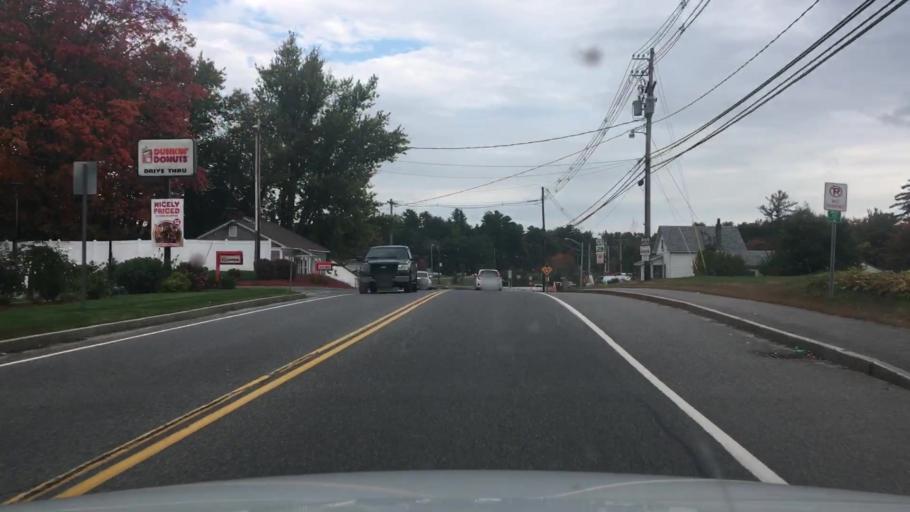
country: US
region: New Hampshire
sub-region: Strafford County
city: New Durham
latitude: 43.4524
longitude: -71.2147
